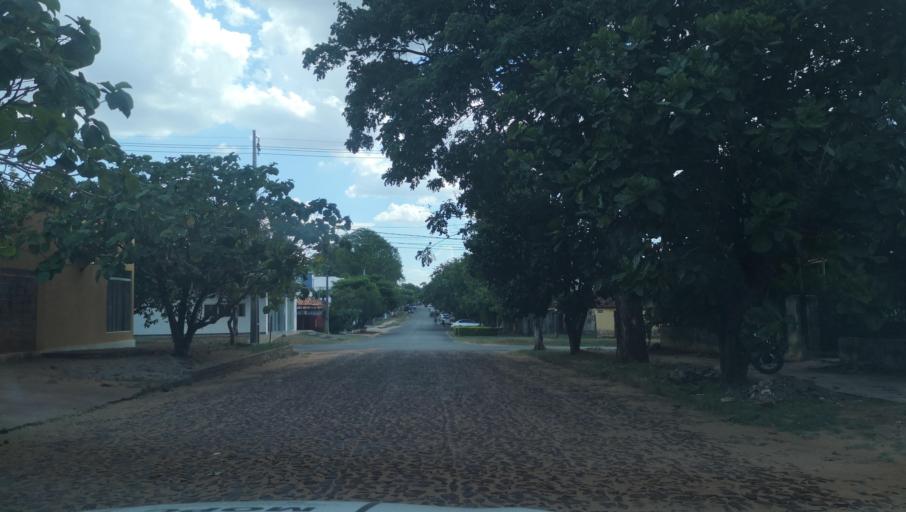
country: PY
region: Misiones
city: Santa Maria
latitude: -26.8899
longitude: -57.0154
